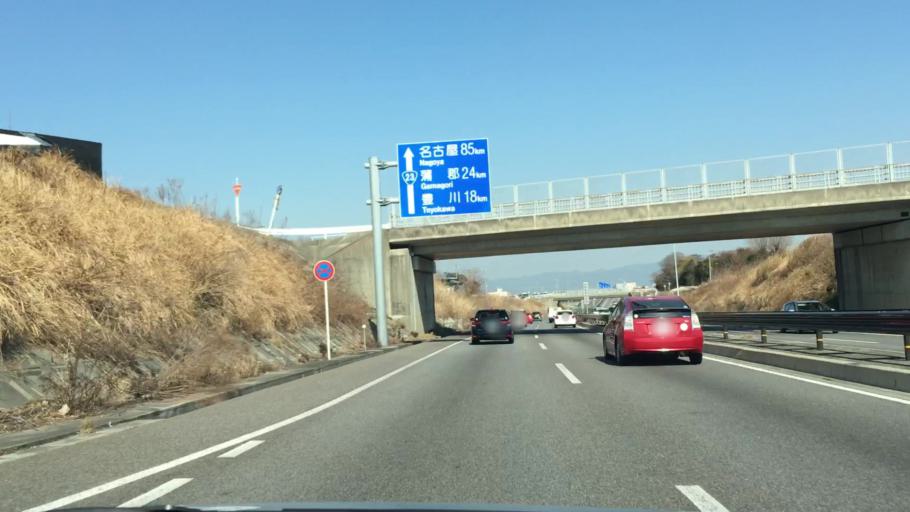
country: JP
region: Aichi
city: Toyohashi
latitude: 34.7135
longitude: 137.3520
